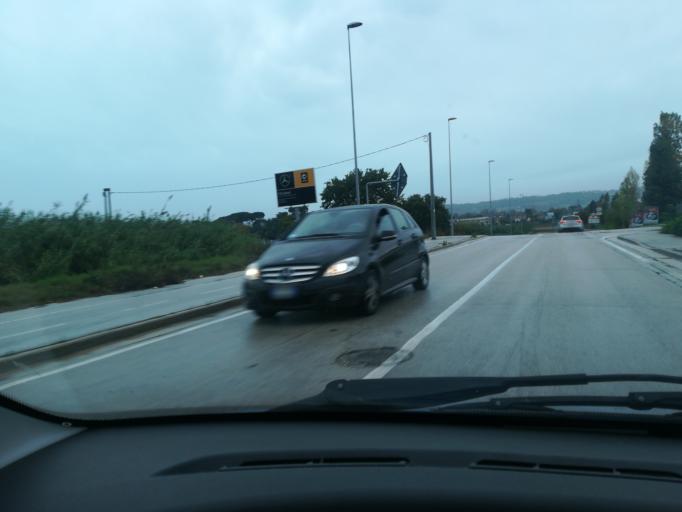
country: IT
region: The Marches
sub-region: Provincia di Macerata
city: Santa Maria Apparente
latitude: 43.2984
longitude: 13.7006
